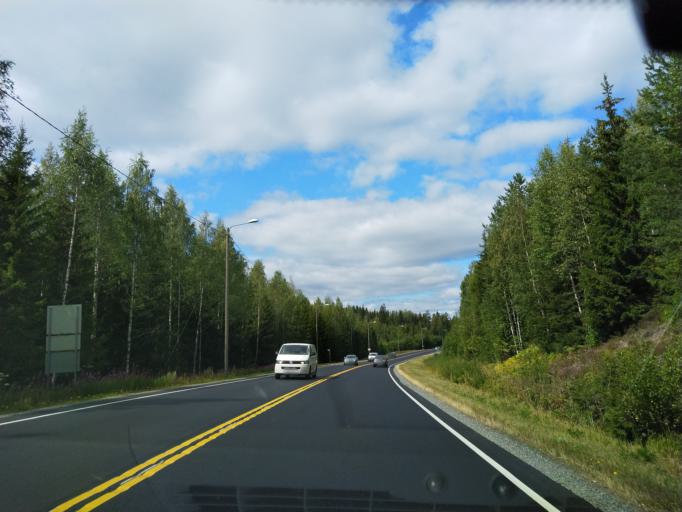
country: FI
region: Haeme
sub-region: Riihimaeki
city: Loppi
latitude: 60.7147
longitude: 24.4713
